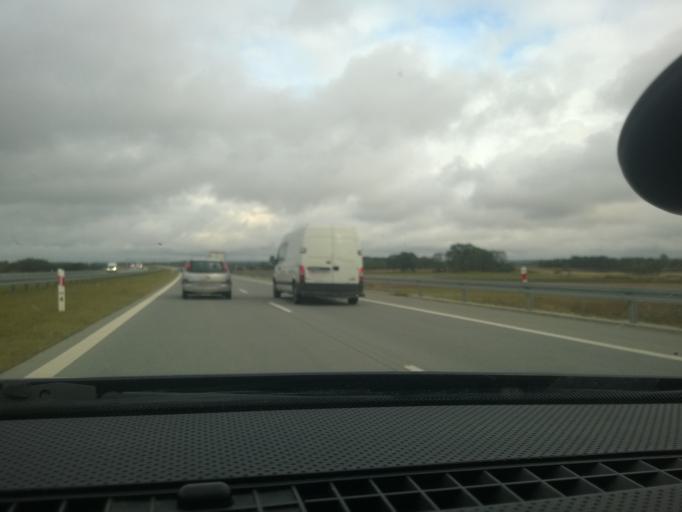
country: PL
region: Lodz Voivodeship
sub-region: Powiat sieradzki
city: Sieradz
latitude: 51.5657
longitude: 18.7724
